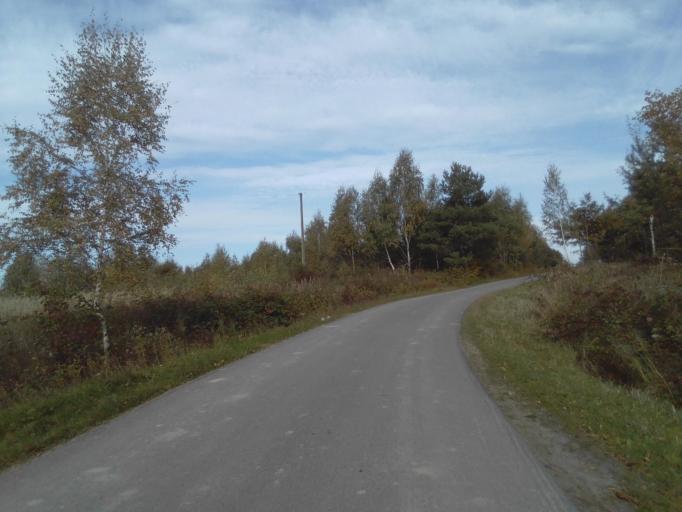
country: PL
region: Subcarpathian Voivodeship
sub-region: Powiat strzyzowski
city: Konieczkowa
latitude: 49.8552
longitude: 21.9575
